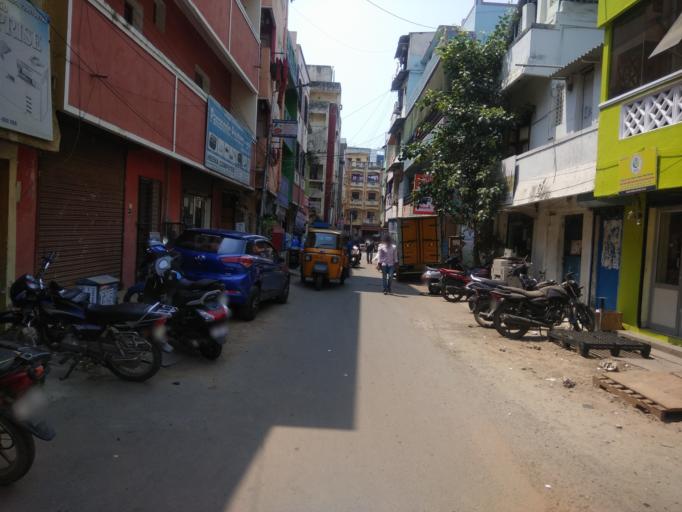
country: IN
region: Tamil Nadu
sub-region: Chennai
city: Chetput
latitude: 13.0556
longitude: 80.2542
